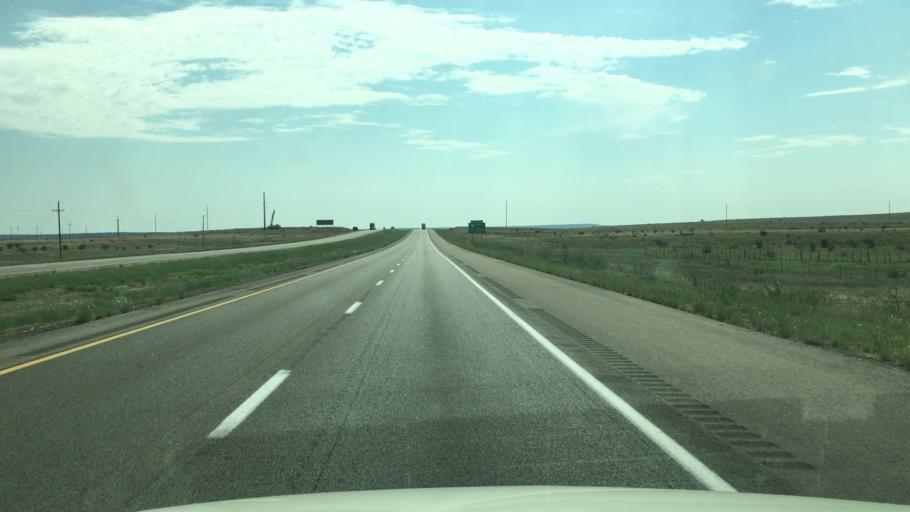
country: US
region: New Mexico
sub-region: Guadalupe County
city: Santa Rosa
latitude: 34.9783
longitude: -105.0315
